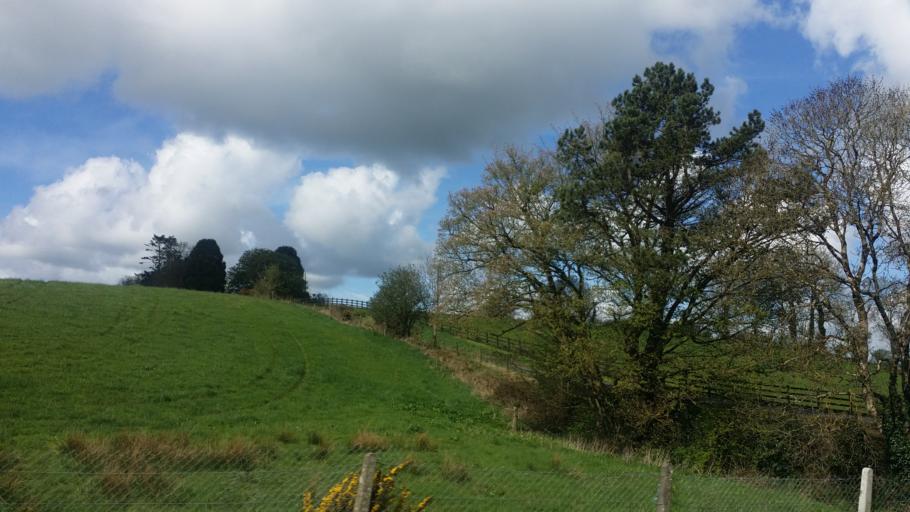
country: IE
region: Ulster
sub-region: An Cabhan
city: Virginia
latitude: 53.8779
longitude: -7.1276
